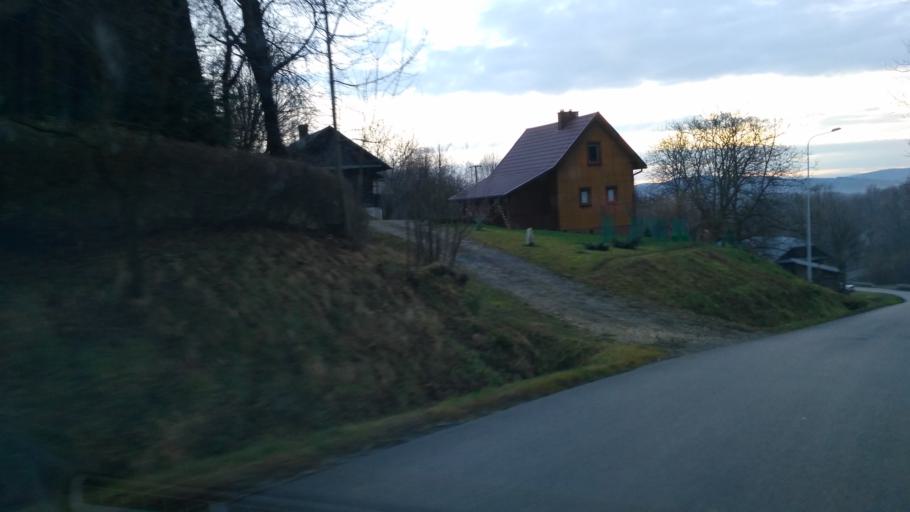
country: PL
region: Subcarpathian Voivodeship
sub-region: Powiat strzyzowski
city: Polomia
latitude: 49.8753
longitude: 21.8637
